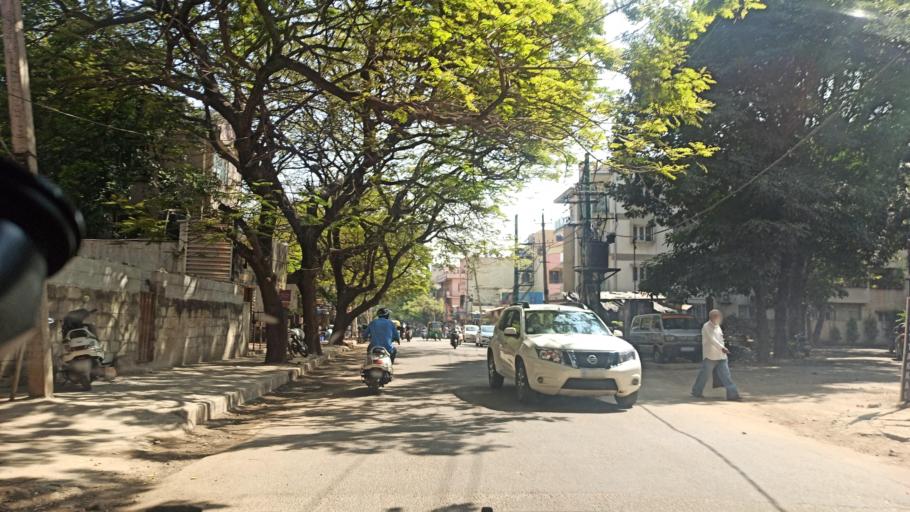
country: IN
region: Karnataka
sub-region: Bangalore Urban
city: Yelahanka
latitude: 13.0427
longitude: 77.5776
